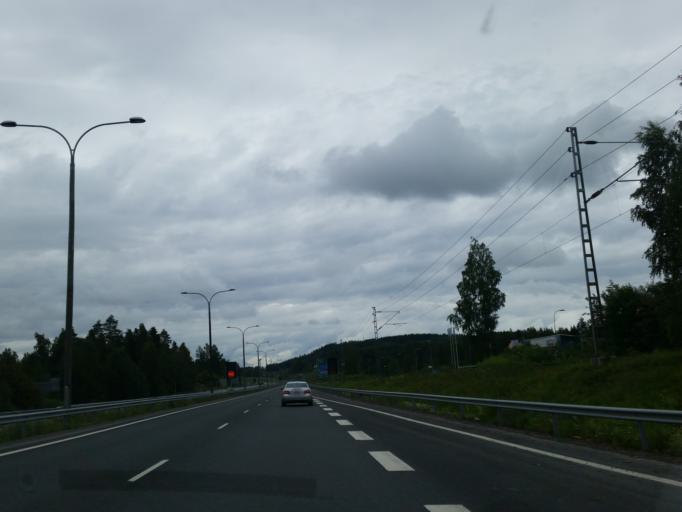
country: FI
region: Northern Savo
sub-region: Kuopio
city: Kuopio
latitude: 62.9625
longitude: 27.6951
